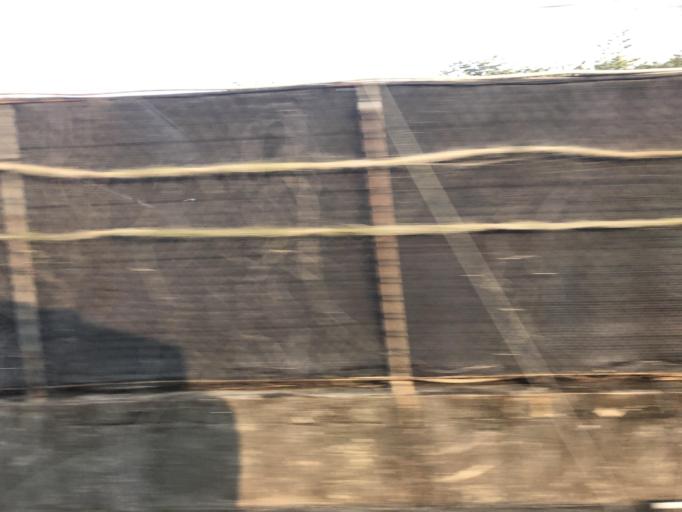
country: TW
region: Taiwan
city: Xinying
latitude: 23.1507
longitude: 120.2742
